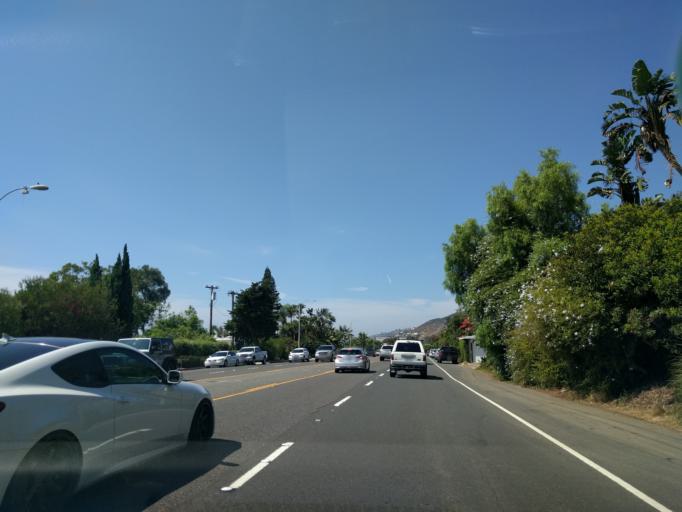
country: US
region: California
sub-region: Orange County
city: Laguna Niguel
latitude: 33.4949
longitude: -117.7374
